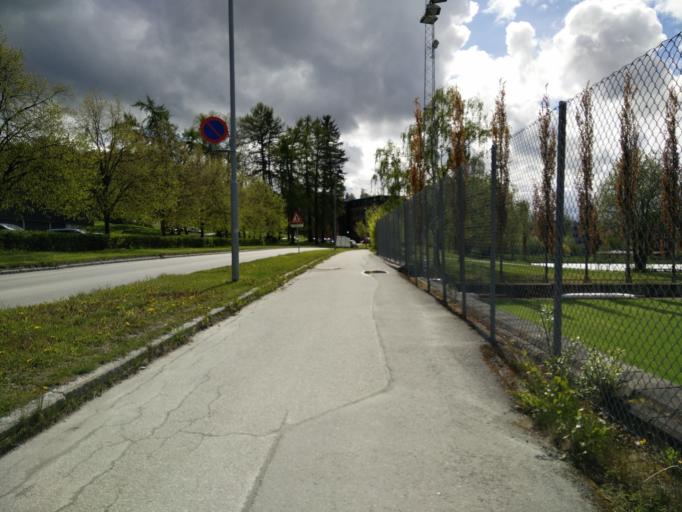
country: NO
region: Sor-Trondelag
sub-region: Trondheim
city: Trondheim
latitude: 63.4108
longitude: 10.4070
